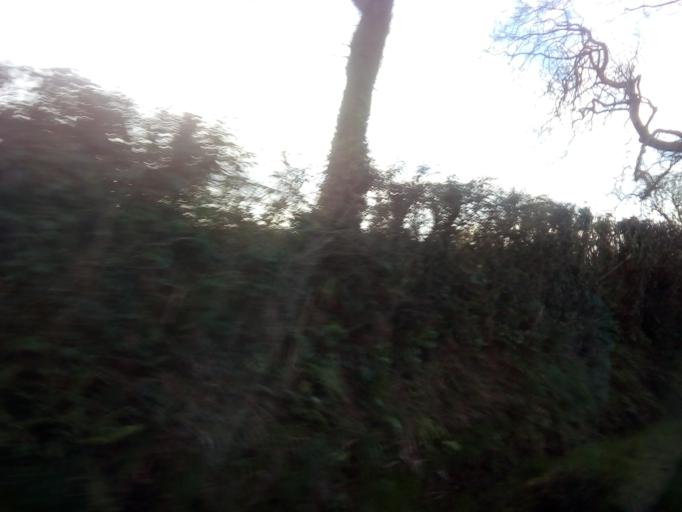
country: IE
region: Leinster
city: Balrothery
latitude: 53.5742
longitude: -6.1496
